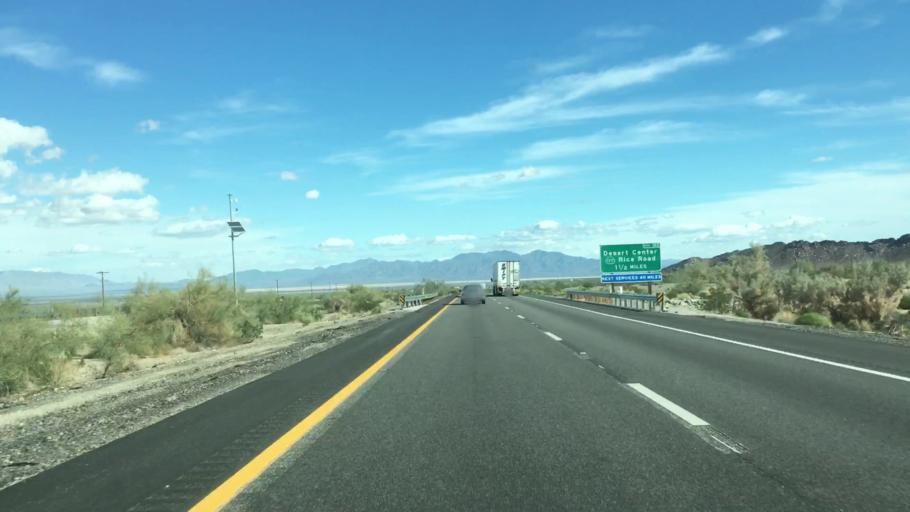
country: US
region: California
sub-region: Imperial County
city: Niland
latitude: 33.7068
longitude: -115.4308
